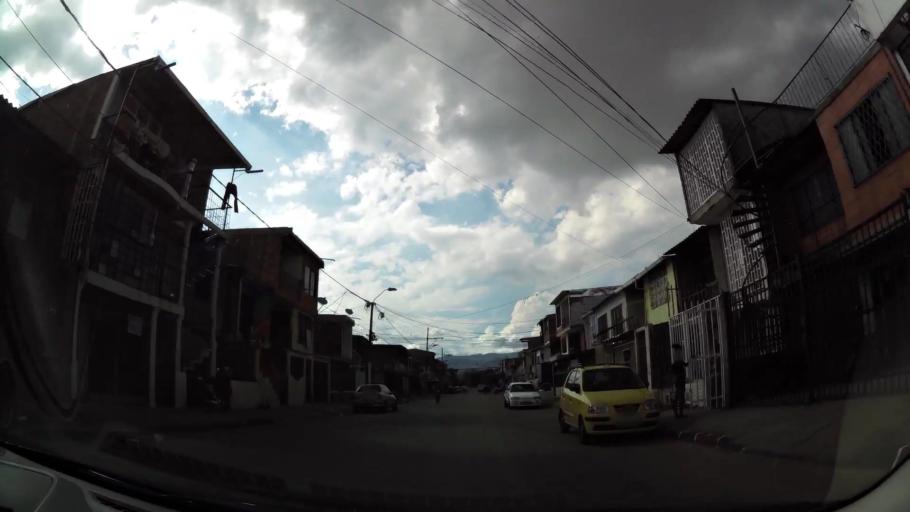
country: CO
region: Valle del Cauca
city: Cali
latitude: 3.4063
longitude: -76.4957
